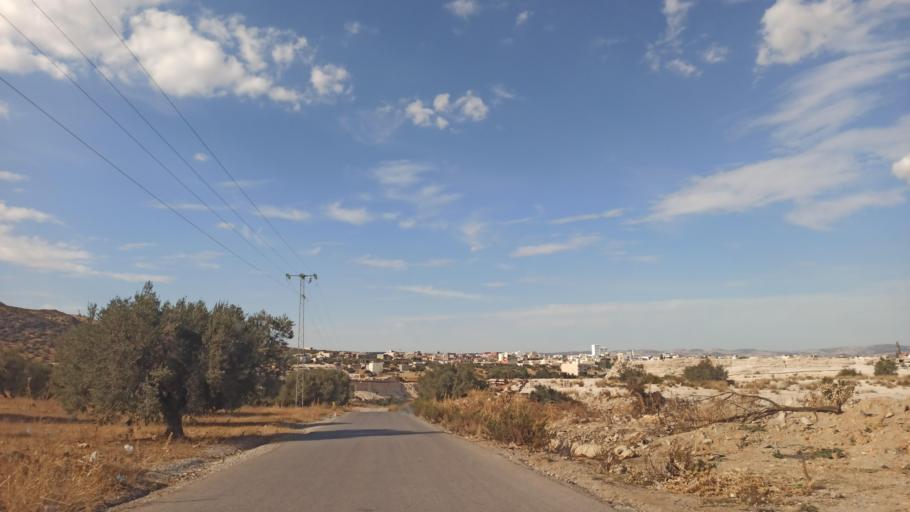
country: TN
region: Zaghwan
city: Zaghouan
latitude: 36.3407
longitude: 10.2090
